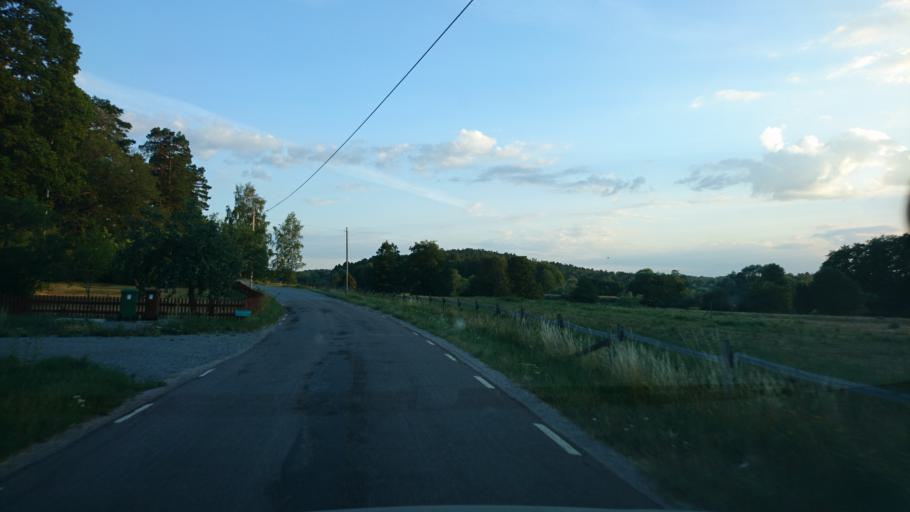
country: SE
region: Uppsala
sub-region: Uppsala Kommun
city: Saevja
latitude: 59.8053
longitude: 17.6718
